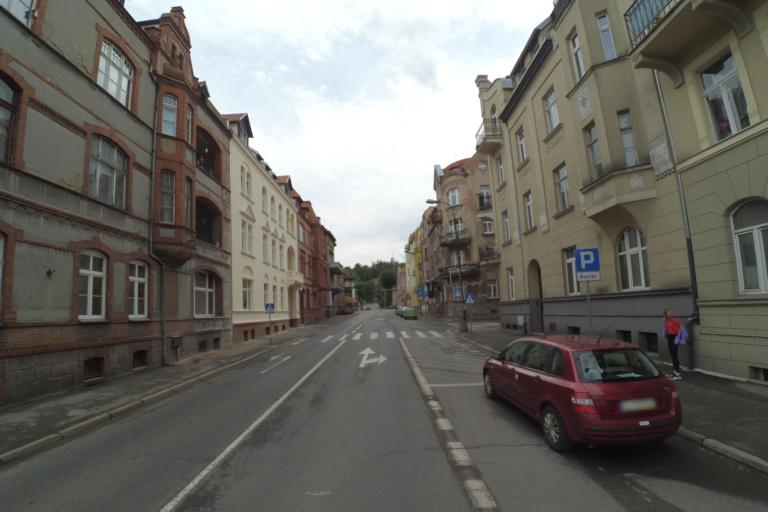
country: PL
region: Lower Silesian Voivodeship
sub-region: Jelenia Gora
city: Jelenia Gora
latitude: 50.8995
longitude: 15.7368
